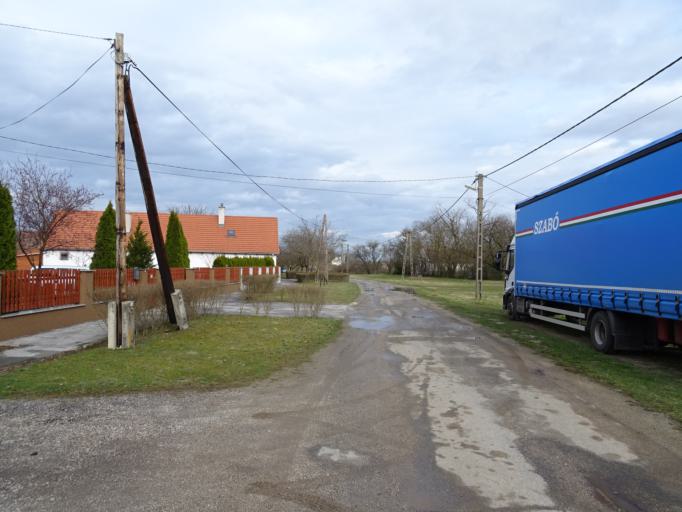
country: HU
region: Gyor-Moson-Sopron
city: Fertoszentmiklos
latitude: 47.4854
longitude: 16.8939
